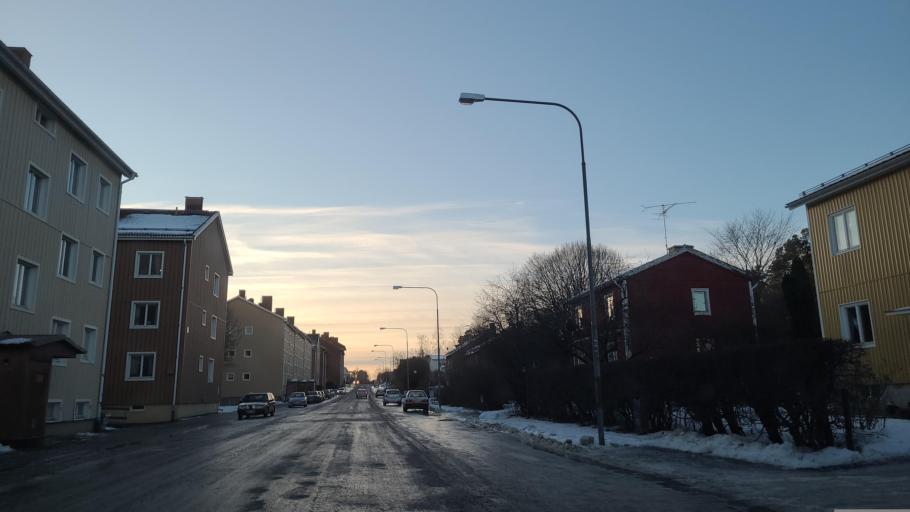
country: SE
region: Gaevleborg
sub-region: Soderhamns Kommun
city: Soderhamn
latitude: 61.3079
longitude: 17.0573
